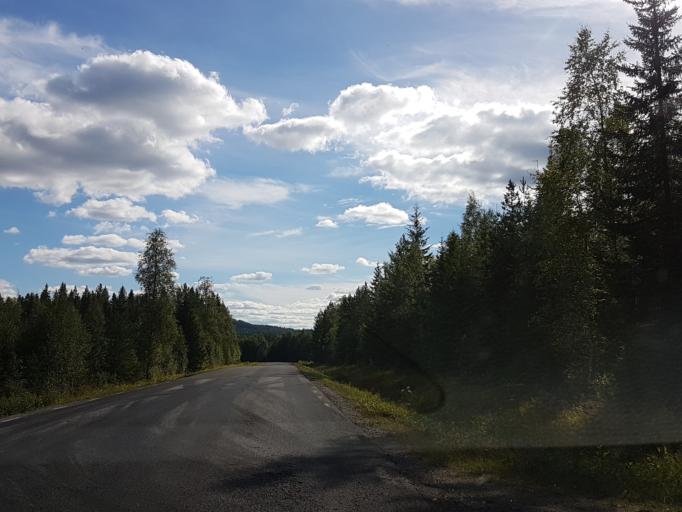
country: SE
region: Vaesterbotten
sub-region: Skelleftea Kommun
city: Burtraesk
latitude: 64.3079
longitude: 20.5300
